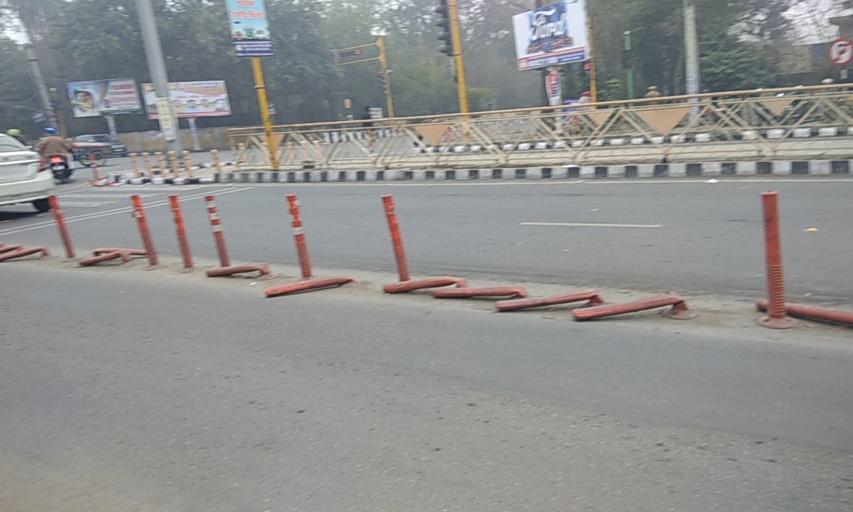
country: IN
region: Punjab
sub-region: Amritsar
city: Amritsar
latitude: 31.6425
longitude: 74.8670
